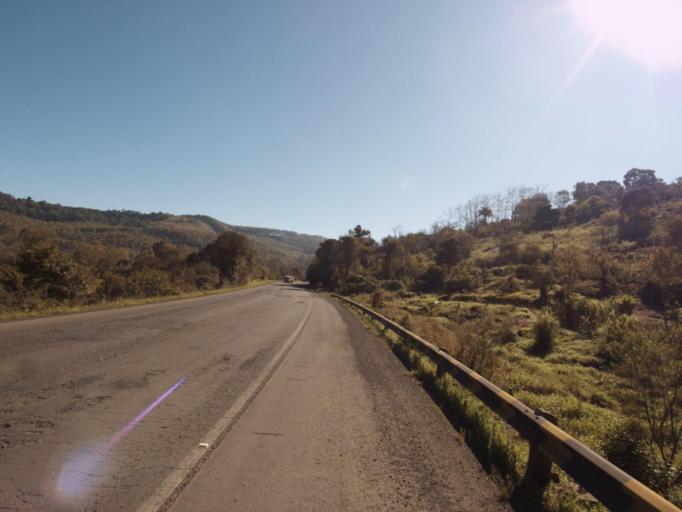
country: BR
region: Rio Grande do Sul
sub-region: Frederico Westphalen
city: Frederico Westphalen
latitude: -27.0210
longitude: -53.2293
